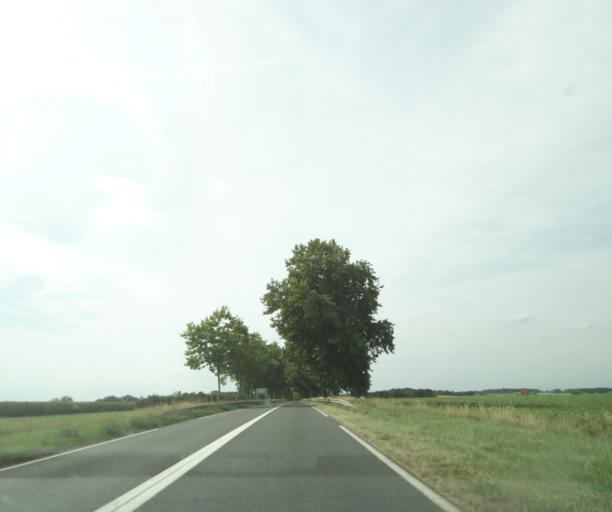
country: FR
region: Centre
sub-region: Departement d'Indre-et-Loire
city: Saint-Paterne-Racan
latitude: 47.5982
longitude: 0.5248
